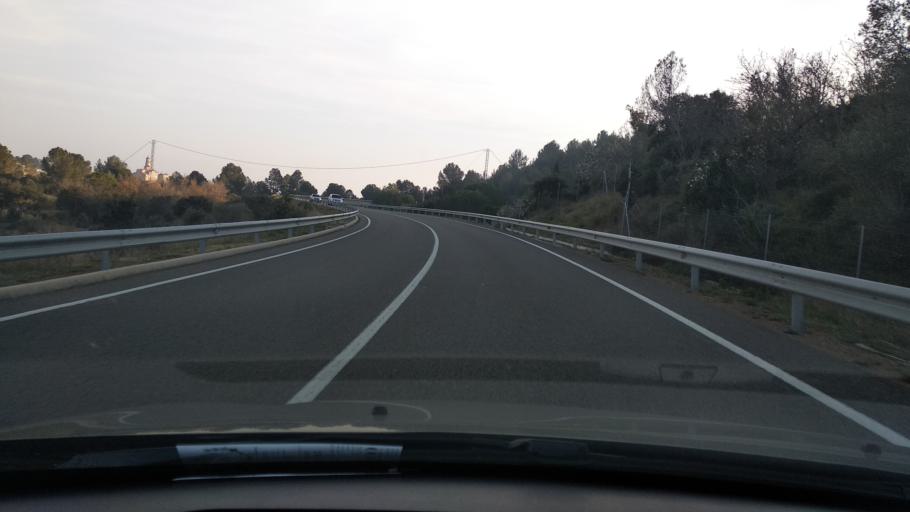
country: ES
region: Catalonia
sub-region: Provincia de Tarragona
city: les Borges del Camp
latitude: 41.1799
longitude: 1.0088
